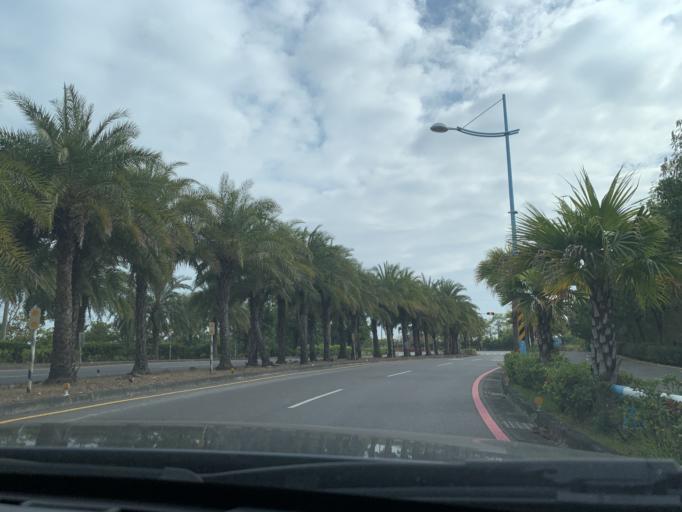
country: TW
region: Taiwan
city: Fengshan
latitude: 22.4552
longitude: 120.4857
